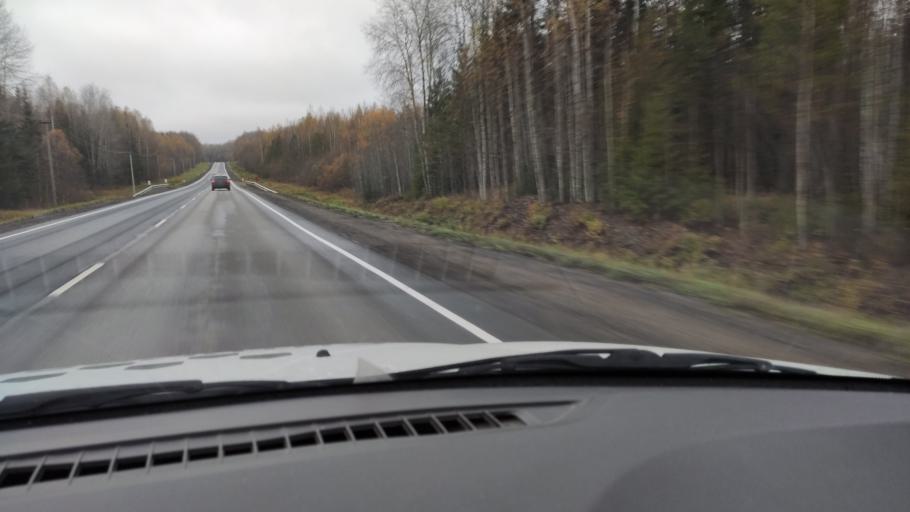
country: RU
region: Kirov
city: Belaya Kholunitsa
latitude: 58.9192
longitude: 51.1288
